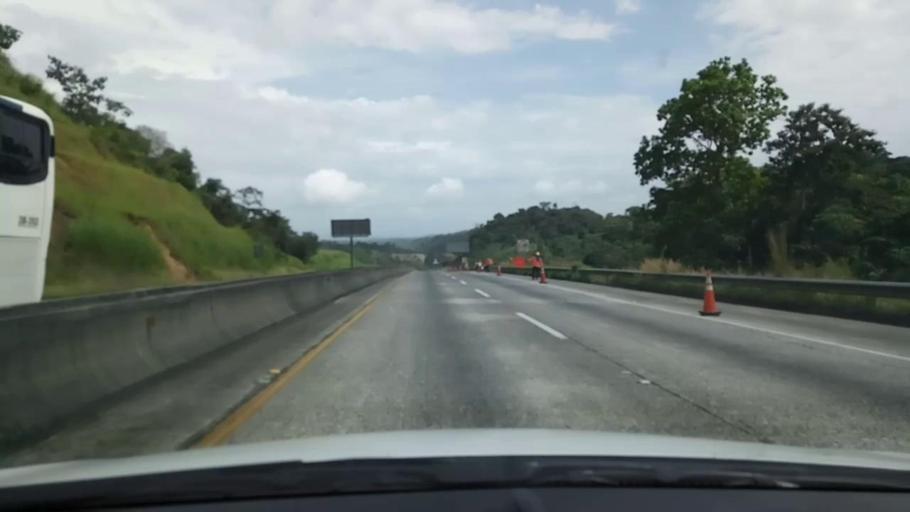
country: PA
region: Colon
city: Quebrada Bonita Adentro
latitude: 9.2826
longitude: -79.7331
